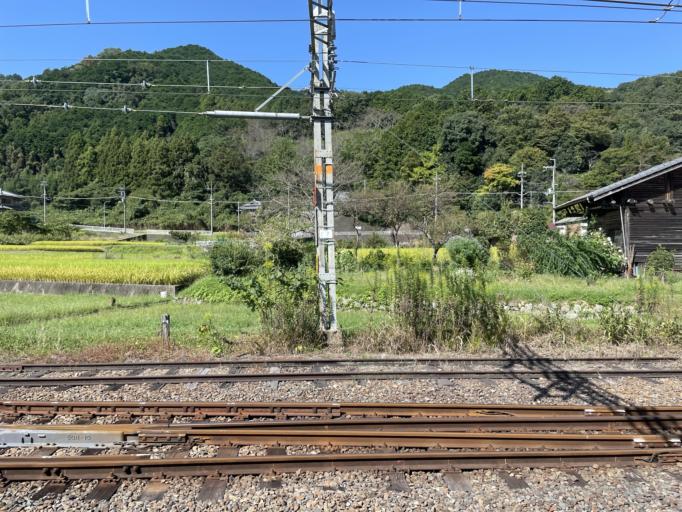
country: JP
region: Nara
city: Gose
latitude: 34.4229
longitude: 135.7510
